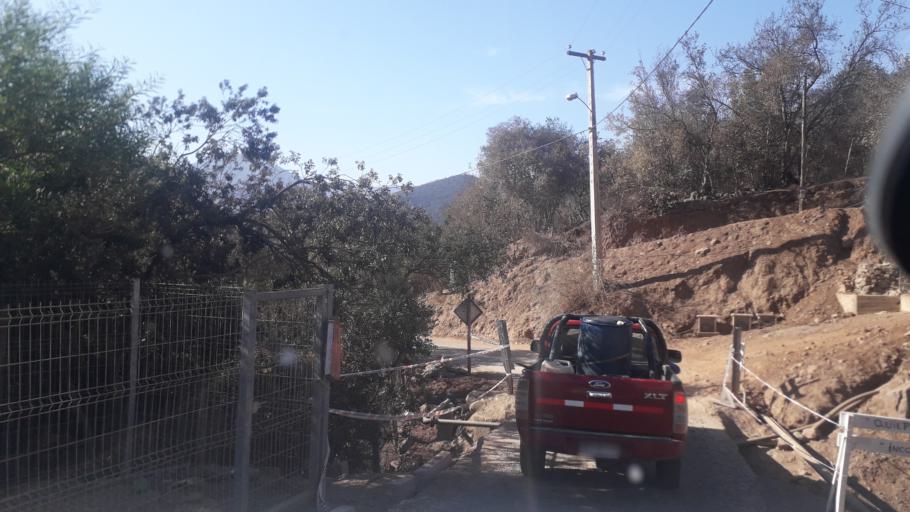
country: CL
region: Valparaiso
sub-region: Provincia de Marga Marga
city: Limache
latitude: -33.0743
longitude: -71.0993
